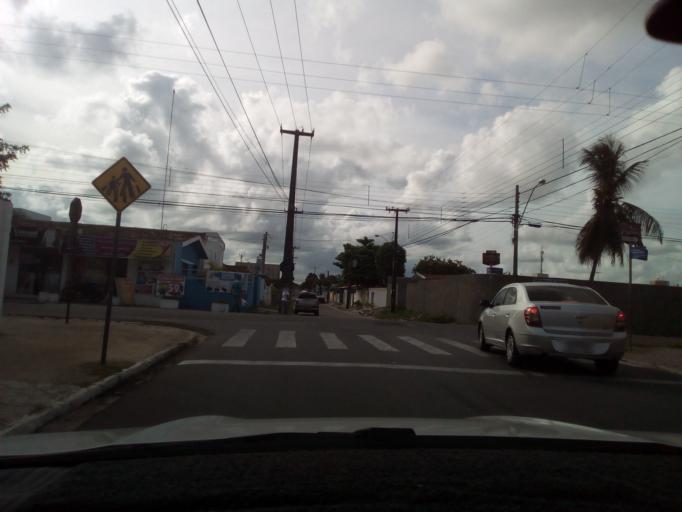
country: BR
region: Paraiba
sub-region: Joao Pessoa
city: Joao Pessoa
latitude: -7.1570
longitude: -34.8738
